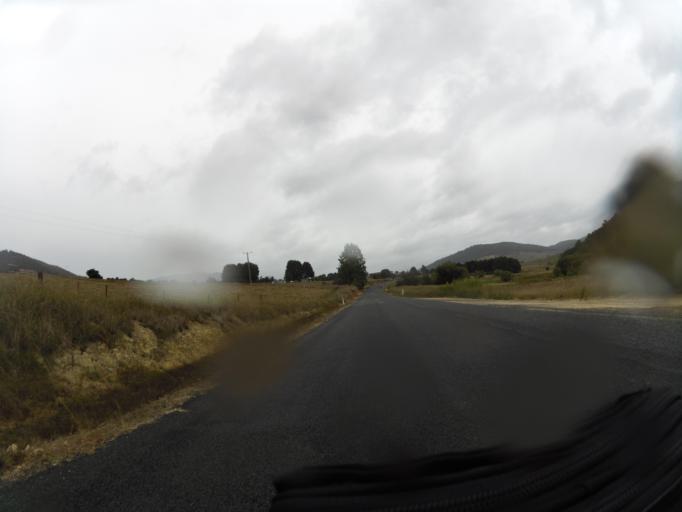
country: AU
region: New South Wales
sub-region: Greater Hume Shire
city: Holbrook
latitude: -36.2289
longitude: 147.6567
